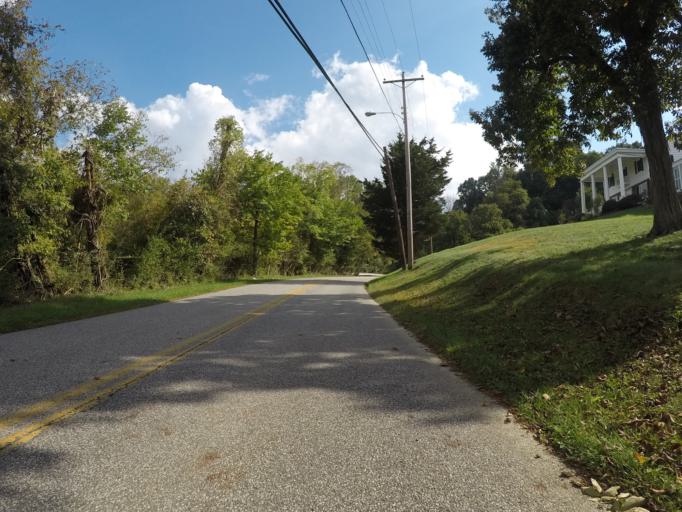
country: US
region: West Virginia
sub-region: Cabell County
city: Huntington
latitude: 38.3997
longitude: -82.4359
